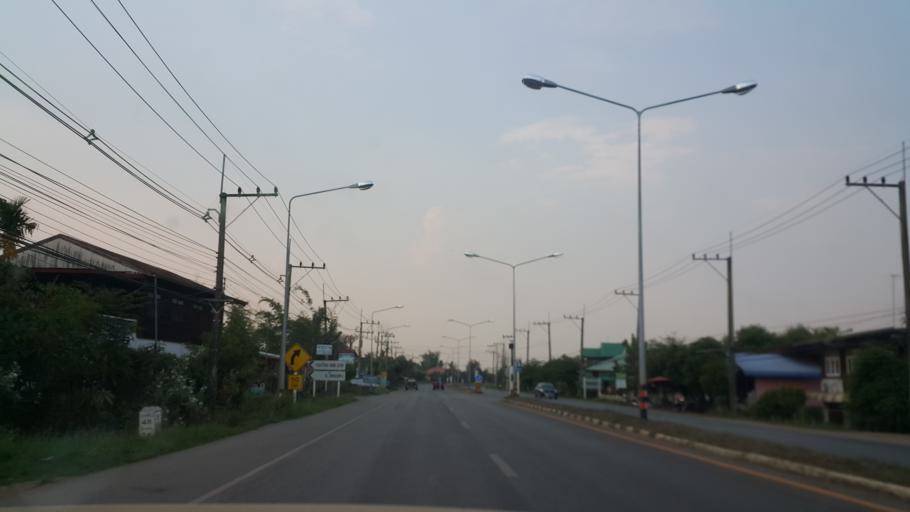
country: TH
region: Nakhon Phanom
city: That Phanom
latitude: 16.9900
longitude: 104.7251
